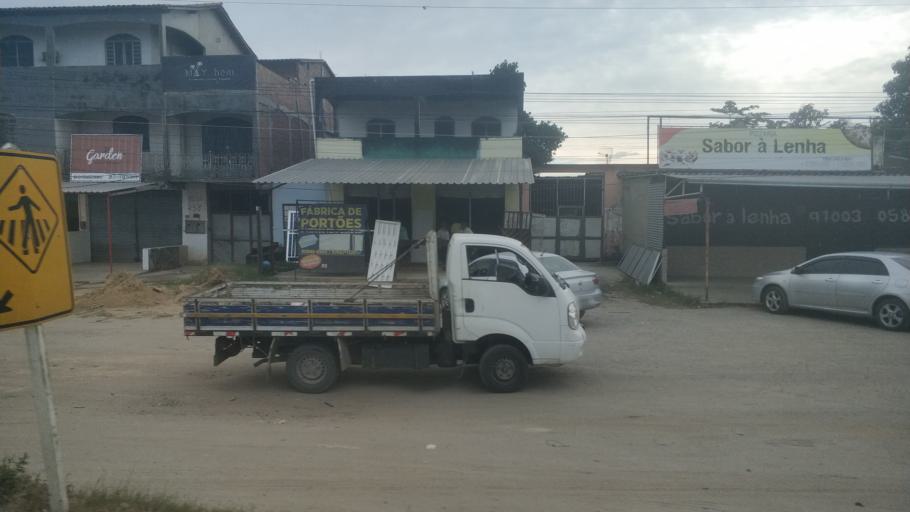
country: BR
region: Rio de Janeiro
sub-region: Seropedica
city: Seropedica
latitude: -22.8031
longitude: -43.6412
